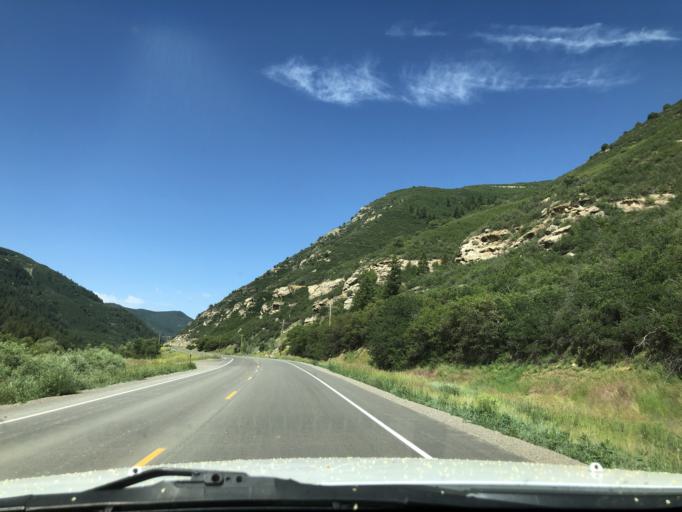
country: US
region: Colorado
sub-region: Delta County
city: Paonia
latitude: 38.9374
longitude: -107.3865
